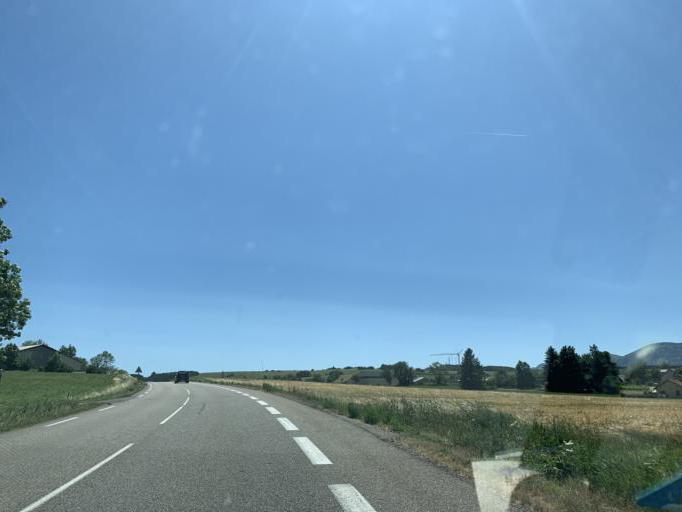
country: FR
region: Provence-Alpes-Cote d'Azur
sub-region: Departement des Hautes-Alpes
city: Saint-Bonnet-en-Champsaur
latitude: 44.6287
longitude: 6.1379
